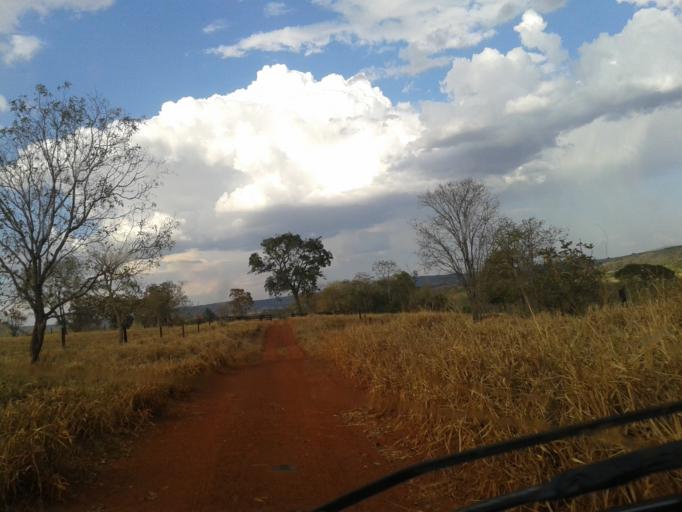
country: BR
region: Minas Gerais
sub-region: Santa Vitoria
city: Santa Vitoria
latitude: -19.1781
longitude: -49.9834
